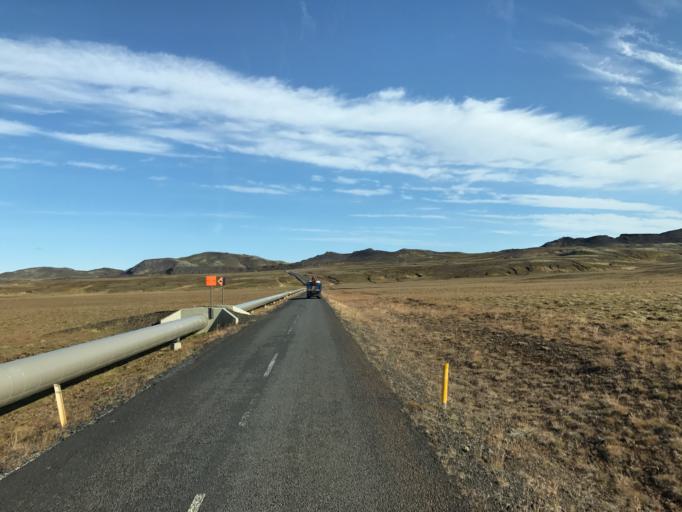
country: IS
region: South
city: Hveragerdi
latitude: 64.1226
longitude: -21.3568
